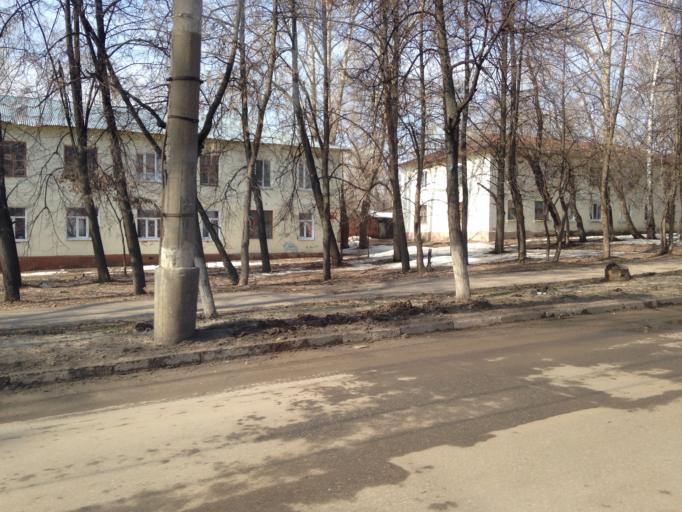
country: RU
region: Ulyanovsk
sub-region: Ulyanovskiy Rayon
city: Ulyanovsk
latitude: 54.3414
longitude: 48.5492
